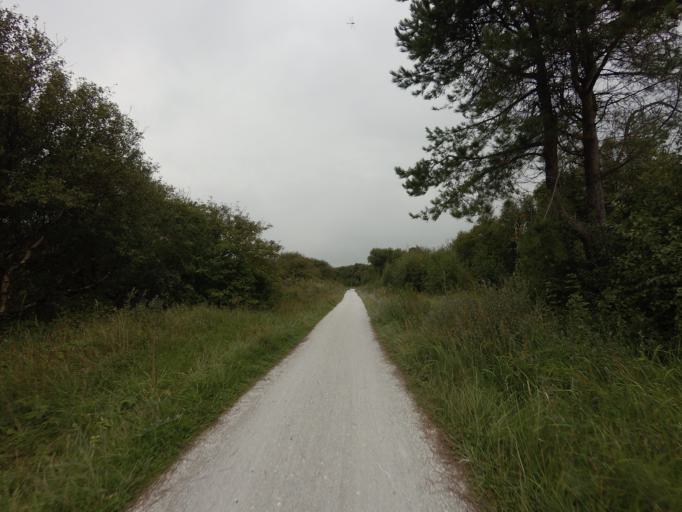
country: NL
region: Friesland
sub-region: Gemeente Schiermonnikoog
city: Schiermonnikoog
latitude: 53.4954
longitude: 6.1732
